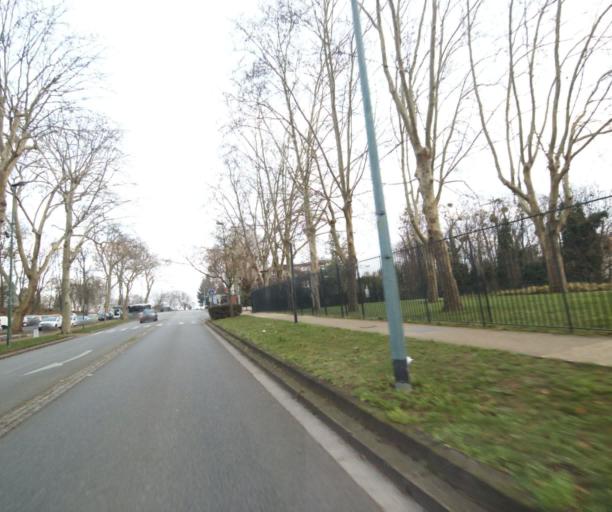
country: FR
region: Ile-de-France
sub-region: Departement des Hauts-de-Seine
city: Suresnes
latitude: 48.8743
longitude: 2.2177
